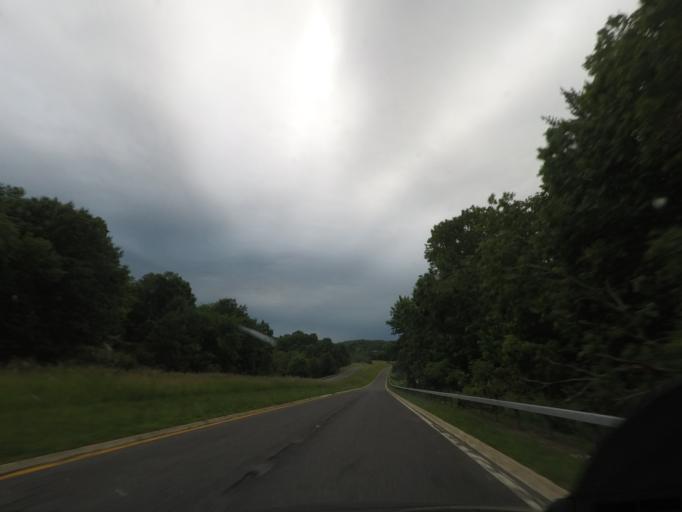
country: US
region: New York
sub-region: Columbia County
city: Chatham
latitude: 42.3472
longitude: -73.5768
